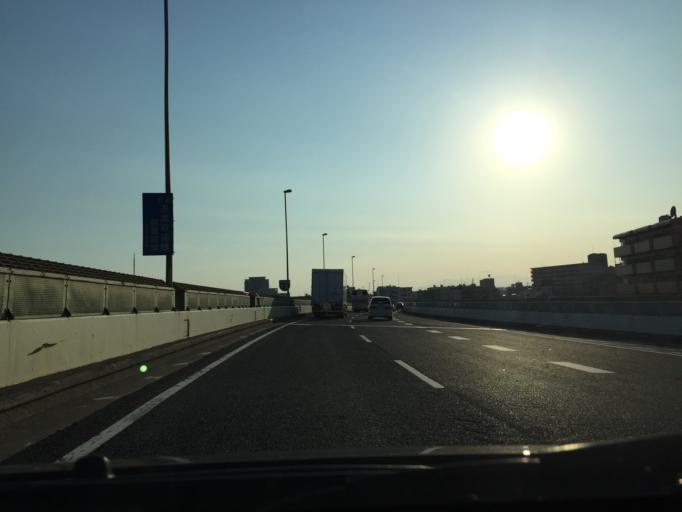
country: JP
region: Kanagawa
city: Yokohama
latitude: 35.4371
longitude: 139.6385
